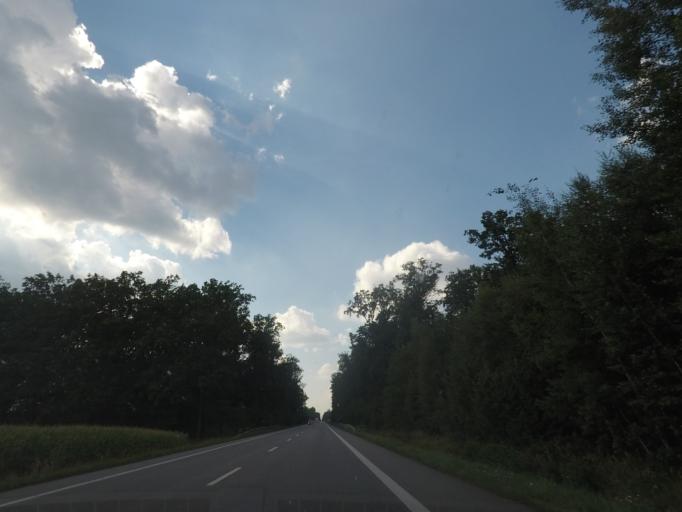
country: CZ
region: Kralovehradecky
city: Trebechovice pod Orebem
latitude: 50.1765
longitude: 16.0292
